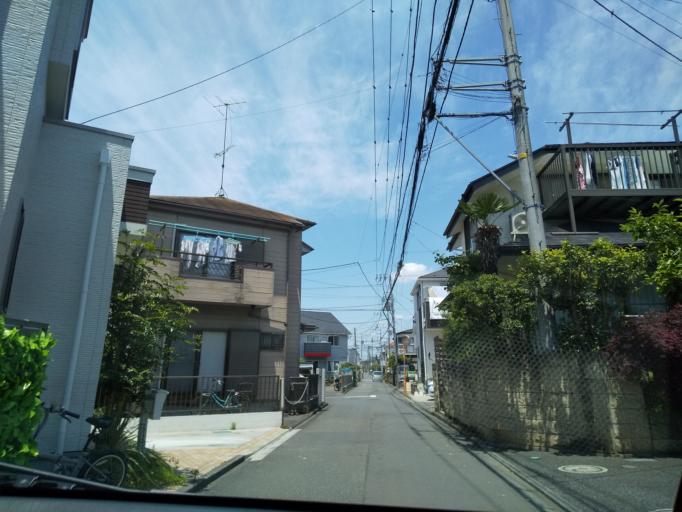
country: JP
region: Tokyo
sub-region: Machida-shi
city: Machida
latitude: 35.5436
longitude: 139.4061
